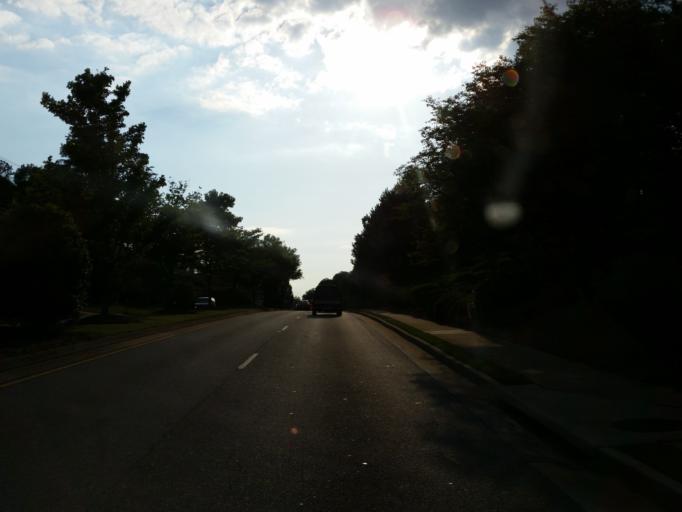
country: US
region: Georgia
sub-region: Cobb County
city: Smyrna
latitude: 33.8836
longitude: -84.4938
